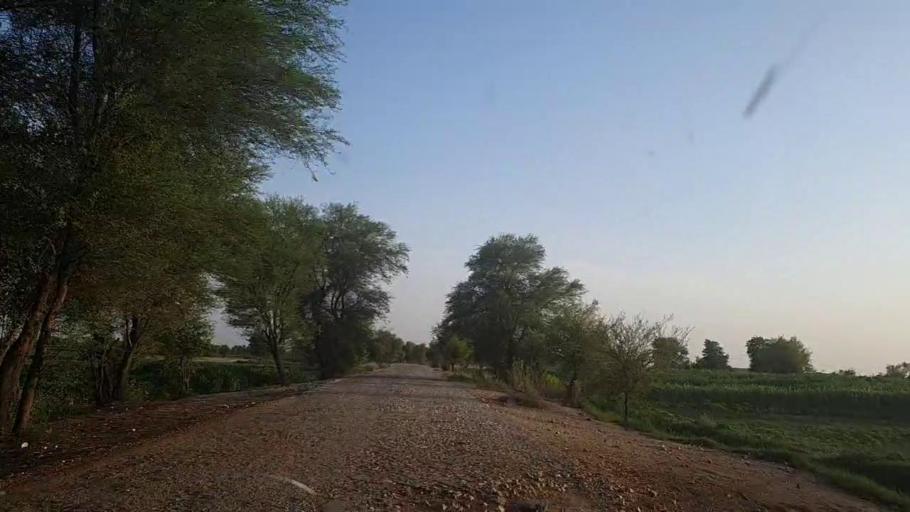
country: PK
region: Sindh
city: Khanpur
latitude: 27.6344
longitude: 69.4480
